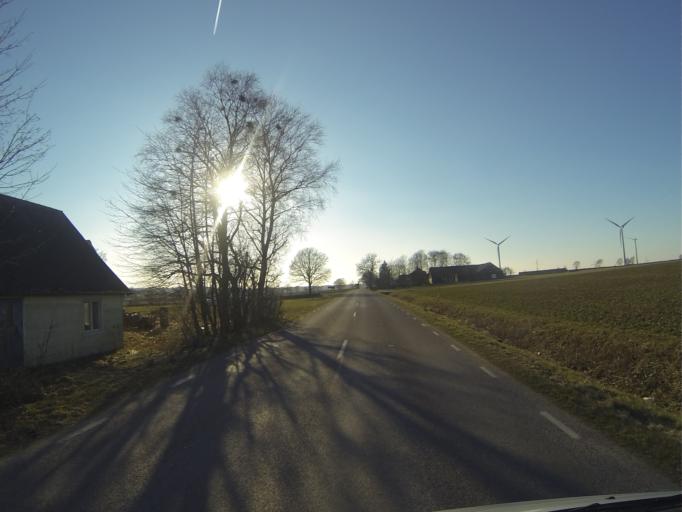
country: SE
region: Skane
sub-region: Hoors Kommun
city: Loberod
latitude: 55.7962
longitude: 13.5592
